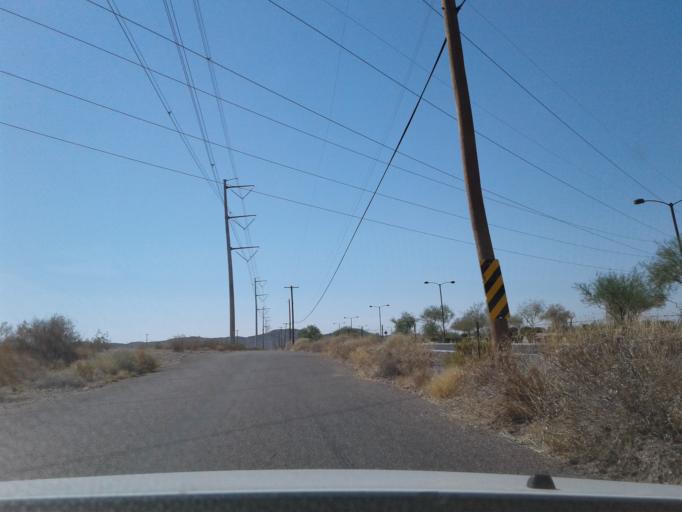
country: US
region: Arizona
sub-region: Maricopa County
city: Laveen
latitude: 33.3214
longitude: -112.1652
